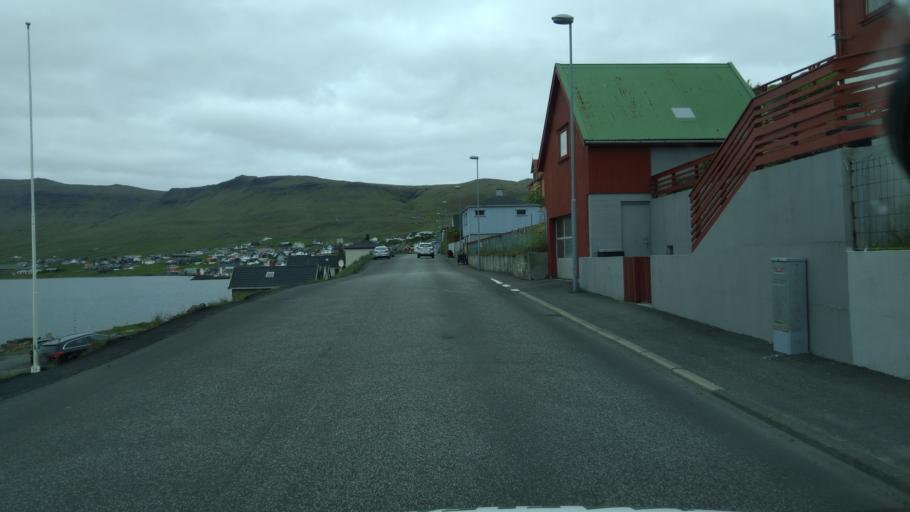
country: FO
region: Suduroy
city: Tvoroyri
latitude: 61.5586
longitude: -6.8218
